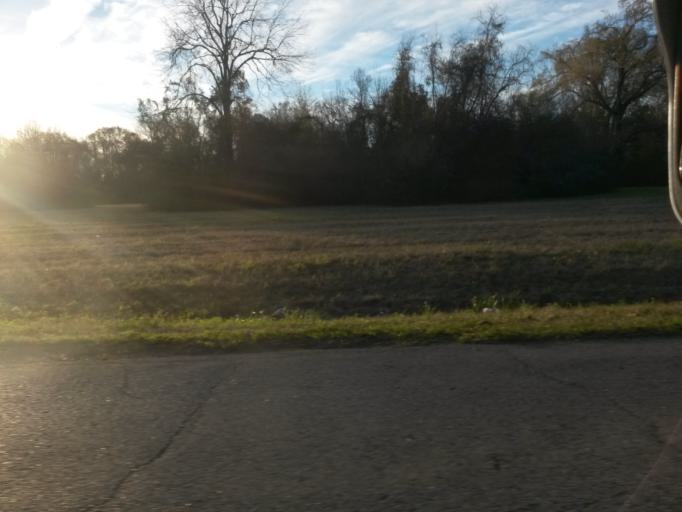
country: US
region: Louisiana
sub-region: Lafayette Parish
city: Lafayette
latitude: 30.2203
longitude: -92.0549
